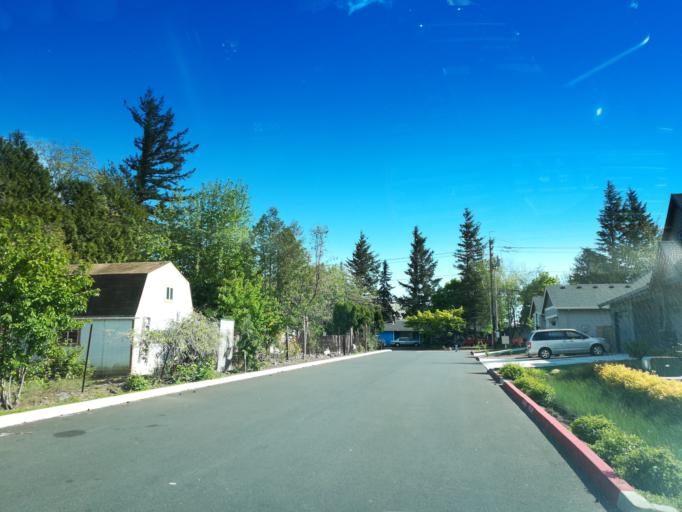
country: US
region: Oregon
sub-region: Multnomah County
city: Troutdale
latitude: 45.5343
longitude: -122.3898
